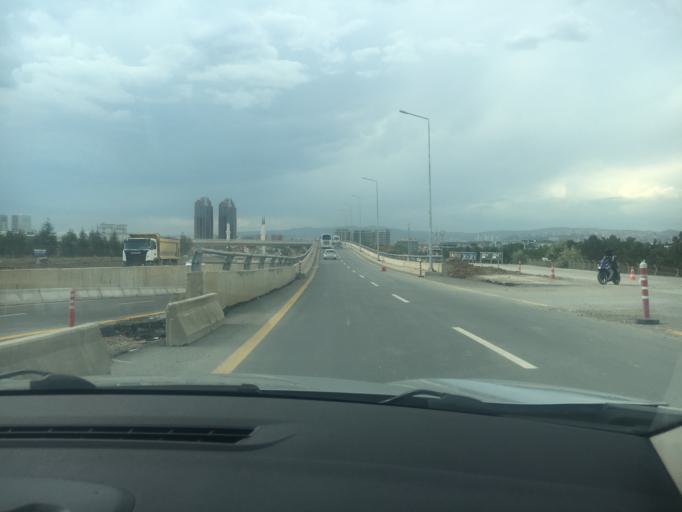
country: TR
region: Ankara
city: Batikent
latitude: 39.8980
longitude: 32.7668
